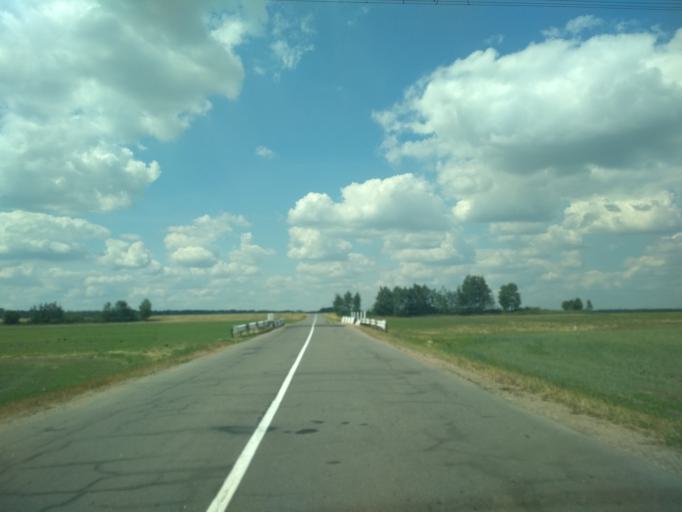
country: BY
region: Minsk
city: Mar''ina Horka
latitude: 53.5597
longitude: 28.0598
